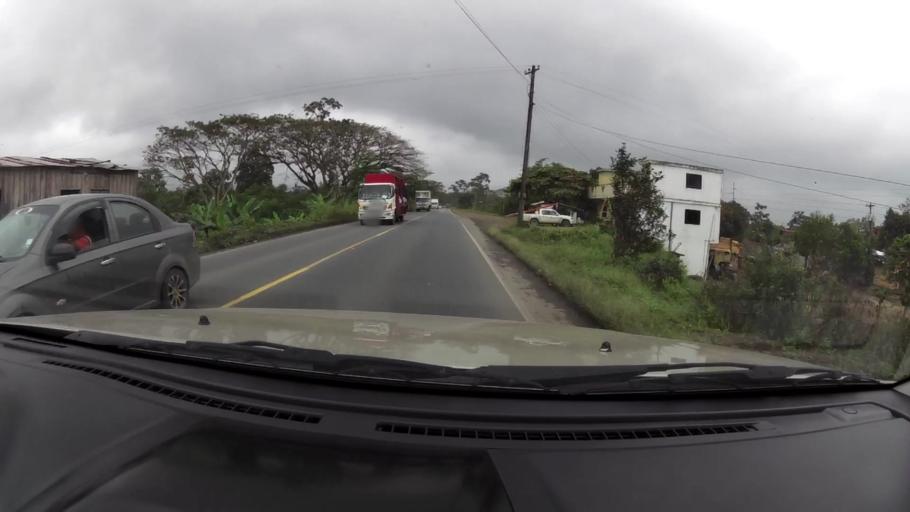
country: EC
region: Guayas
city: Balao
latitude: -2.9811
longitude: -79.7264
